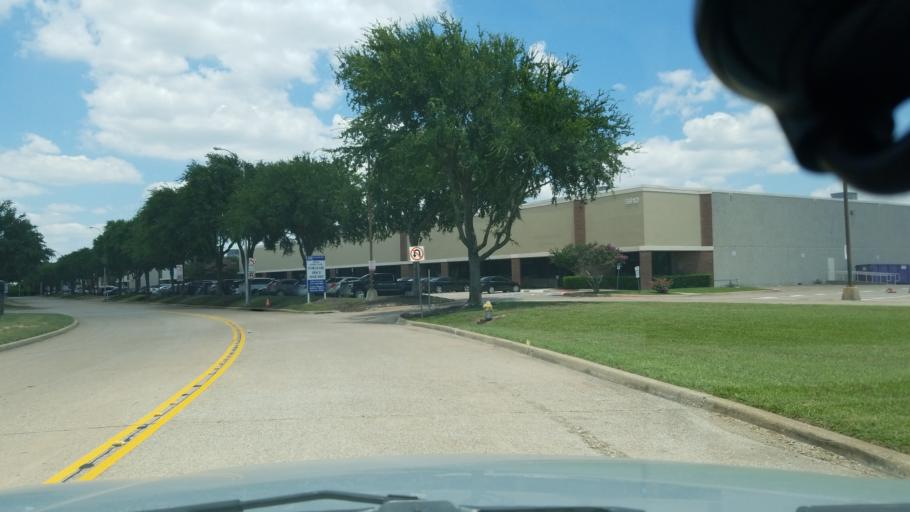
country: US
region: Texas
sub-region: Dallas County
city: Duncanville
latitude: 32.6778
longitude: -96.8803
